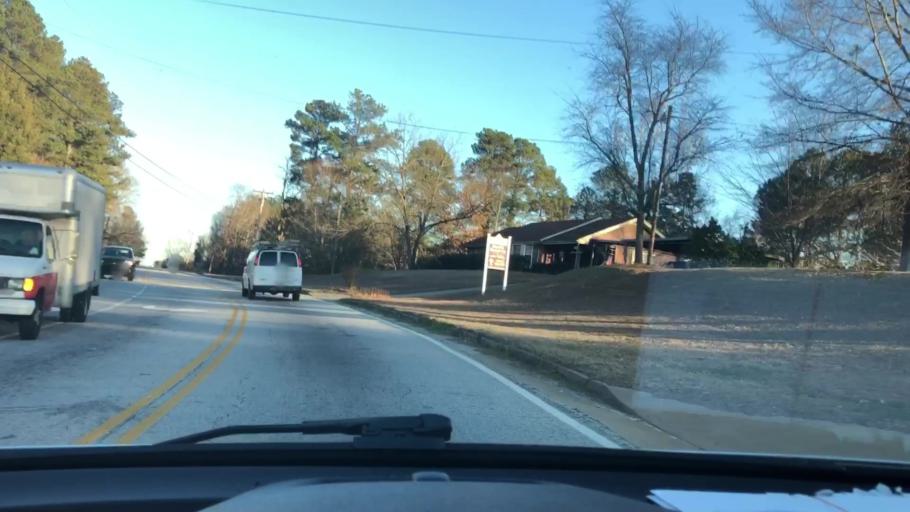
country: US
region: Georgia
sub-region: DeKalb County
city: Lithonia
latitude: 33.7348
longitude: -84.0874
